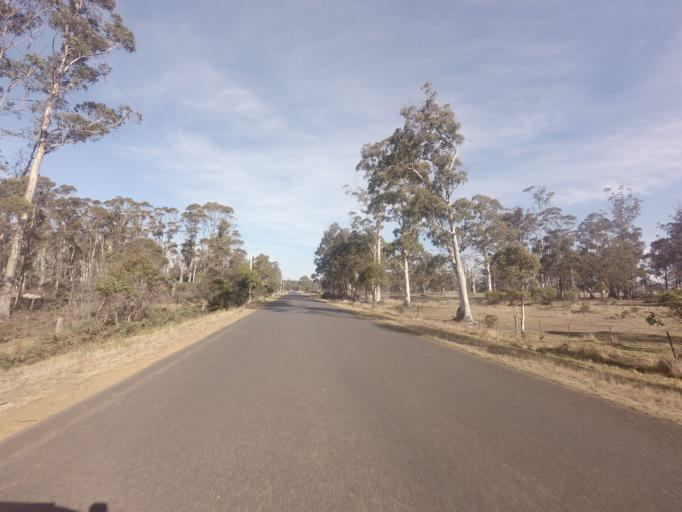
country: AU
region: Tasmania
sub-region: Sorell
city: Sorell
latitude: -42.4650
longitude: 147.4613
